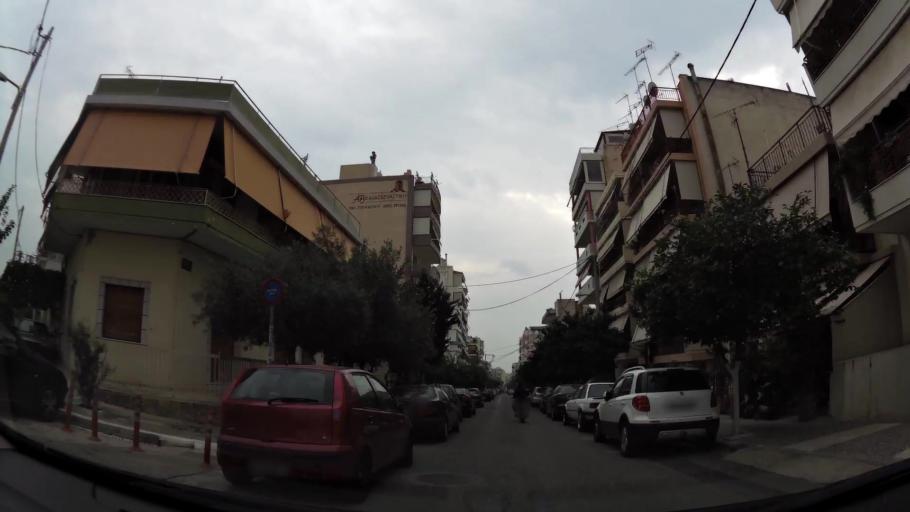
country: GR
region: Attica
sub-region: Nomos Piraios
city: Korydallos
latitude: 37.9806
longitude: 23.6343
